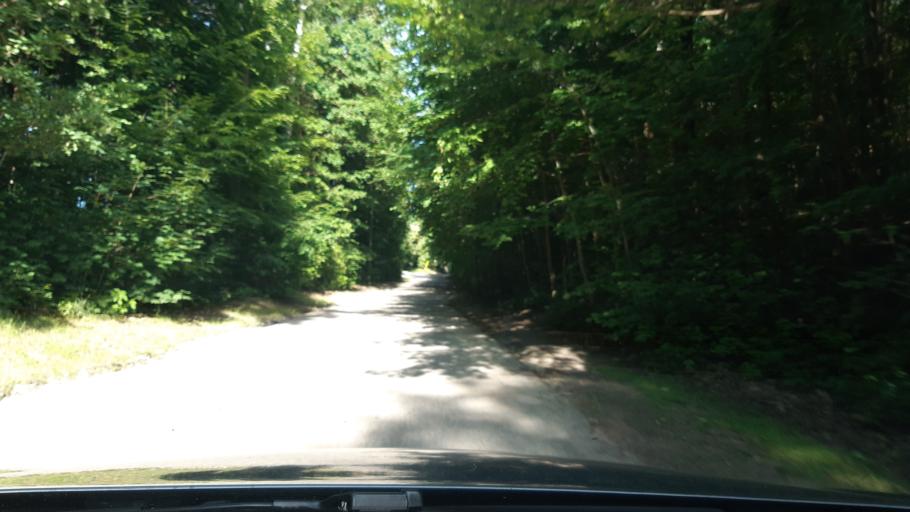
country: PL
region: Warmian-Masurian Voivodeship
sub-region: Powiat mragowski
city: Mragowo
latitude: 53.8730
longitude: 21.3233
